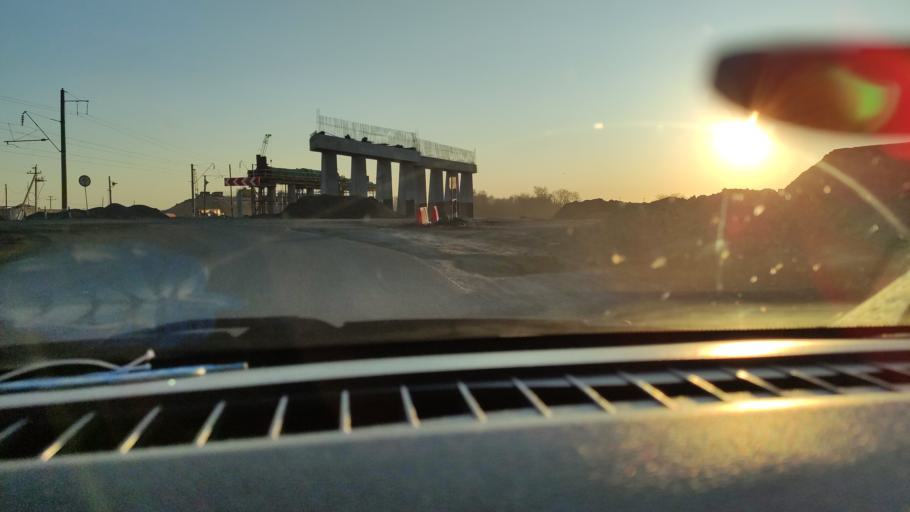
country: RU
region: Saratov
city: Sinodskoye
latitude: 52.0101
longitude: 46.6881
